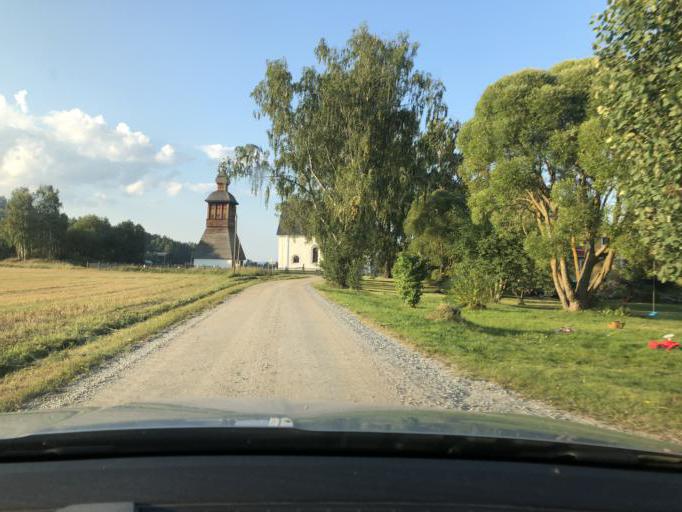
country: SE
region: Vaesternorrland
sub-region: Kramfors Kommun
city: Bollstabruk
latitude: 63.0786
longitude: 17.7410
